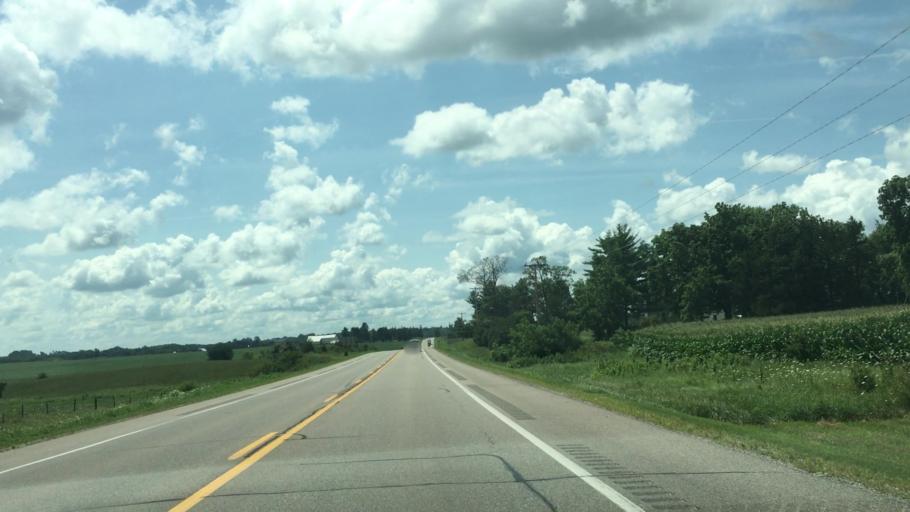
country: US
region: Iowa
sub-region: Johnson County
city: Solon
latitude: 41.8310
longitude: -91.4983
